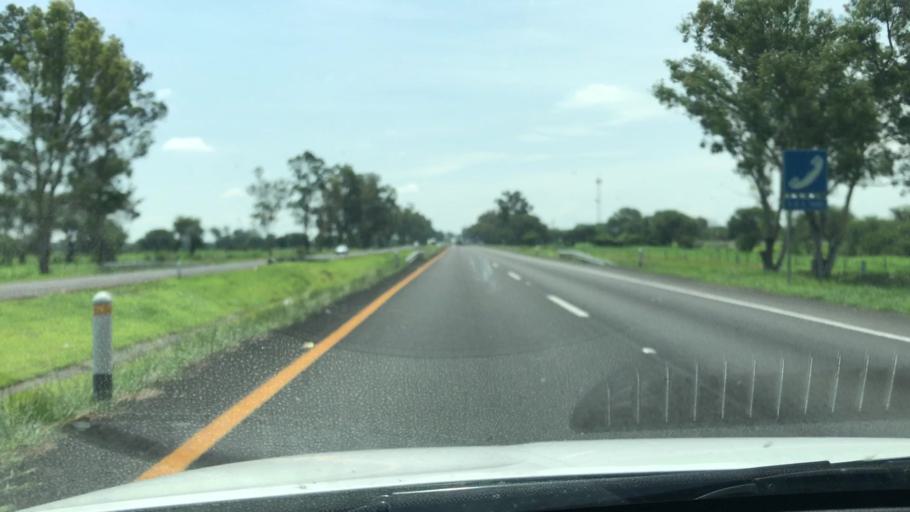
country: MX
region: Jalisco
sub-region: Ocotlan
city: Joconoxtle (La Tuna)
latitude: 20.3760
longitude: -102.6732
